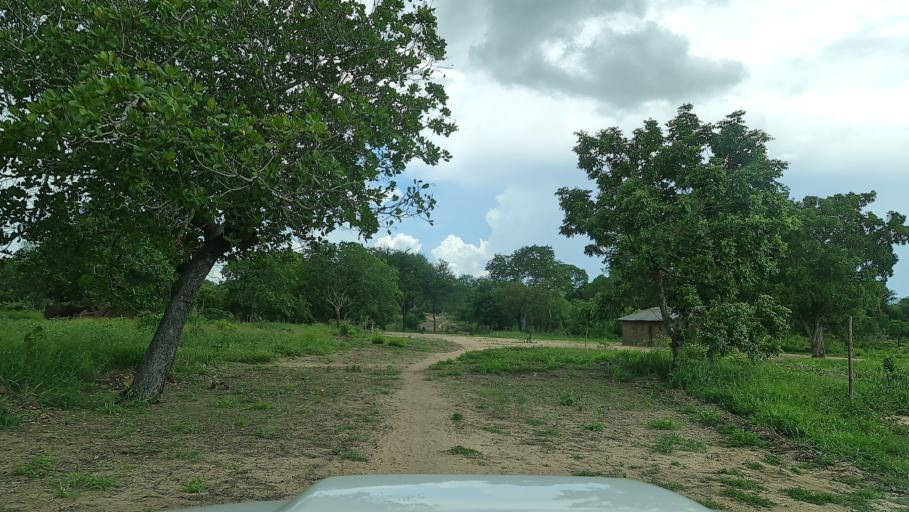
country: MZ
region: Nampula
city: Ilha de Mocambique
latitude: -15.4997
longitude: 40.1591
